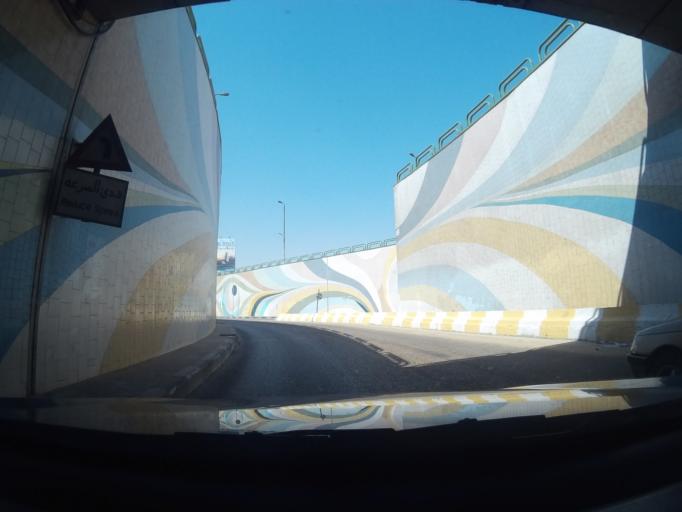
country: EG
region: Muhafazat al Qahirah
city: Cairo
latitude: 29.9994
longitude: 31.4020
